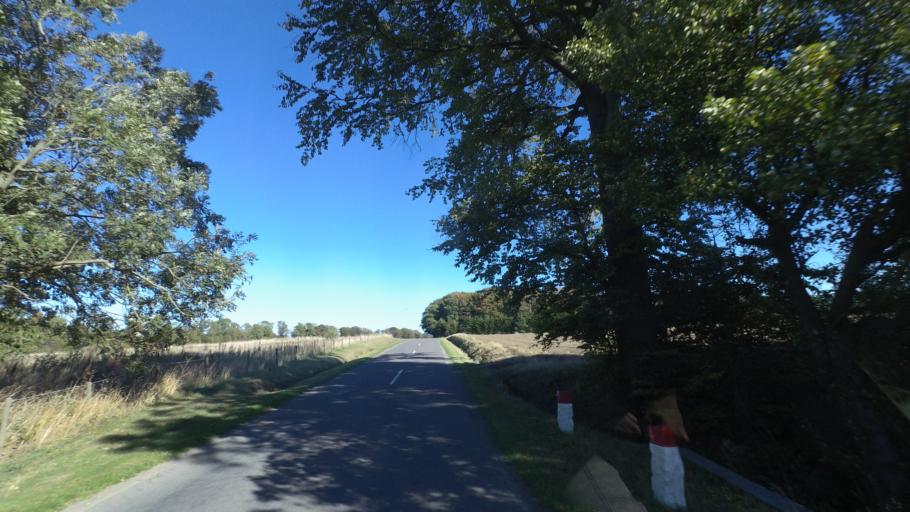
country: DK
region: Capital Region
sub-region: Bornholm Kommune
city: Nexo
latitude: 55.1105
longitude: 15.1189
